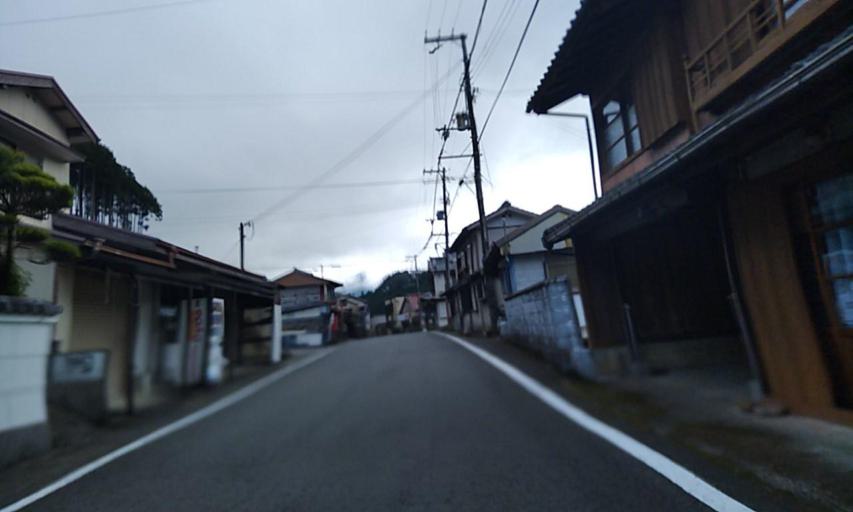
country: JP
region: Wakayama
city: Shingu
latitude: 33.9309
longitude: 135.9654
